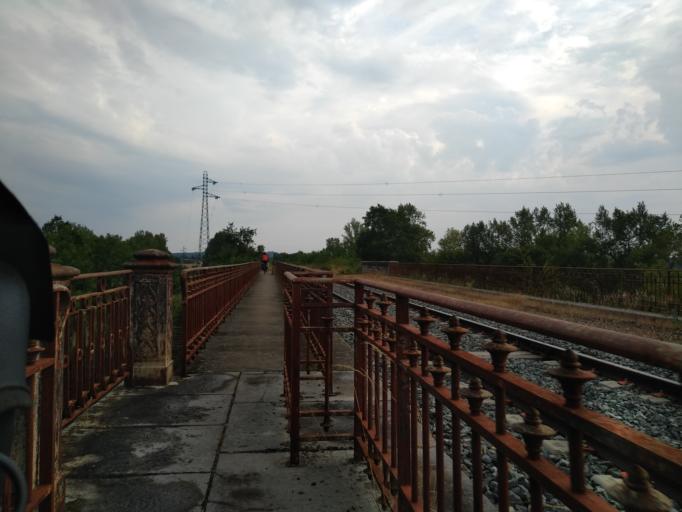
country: FR
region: Auvergne
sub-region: Departement de l'Allier
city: Varennes-sur-Allier
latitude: 46.3489
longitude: 3.3467
